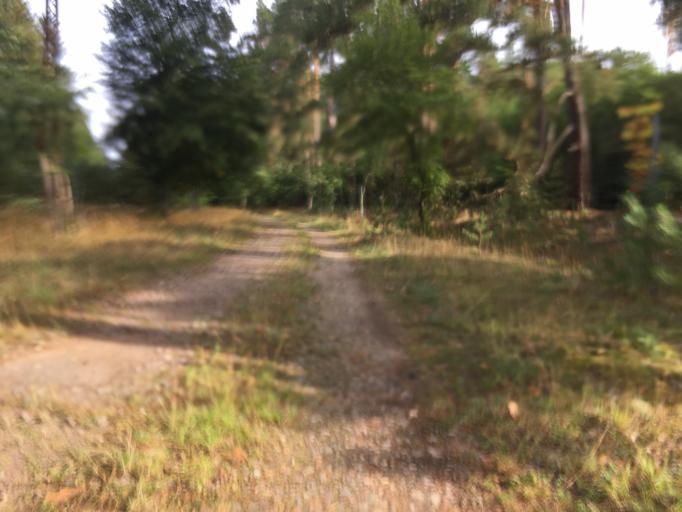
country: DE
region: Brandenburg
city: Marienwerder
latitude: 52.9717
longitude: 13.5308
